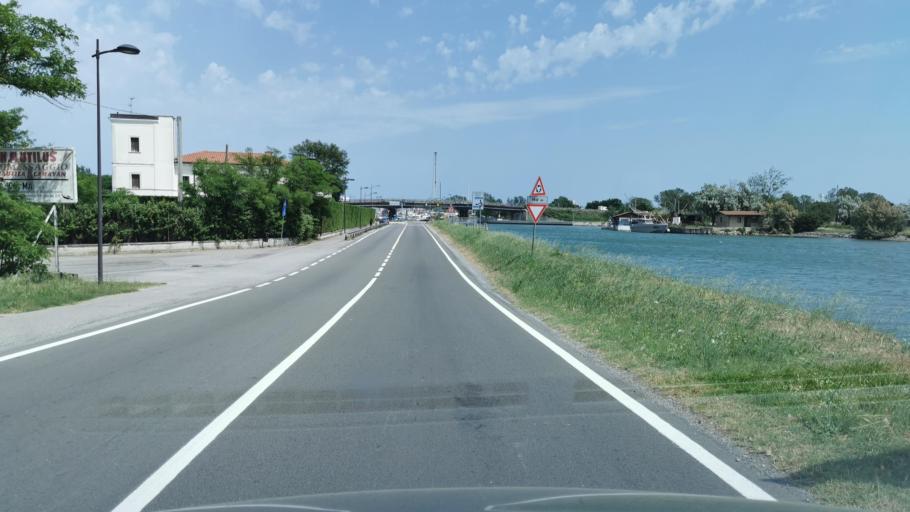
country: IT
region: Emilia-Romagna
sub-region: Provincia di Ferrara
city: Porto Garibaldi
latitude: 44.6760
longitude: 12.2237
